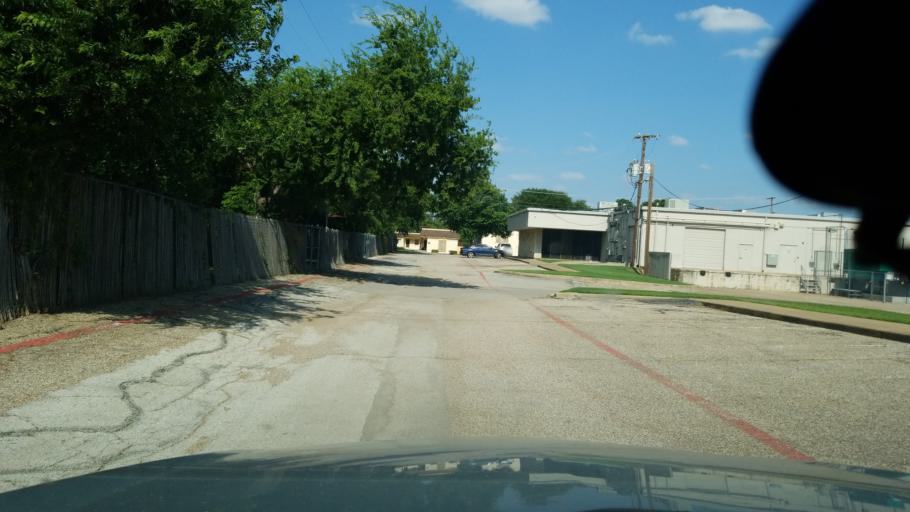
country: US
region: Texas
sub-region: Dallas County
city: Irving
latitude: 32.8175
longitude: -96.9750
